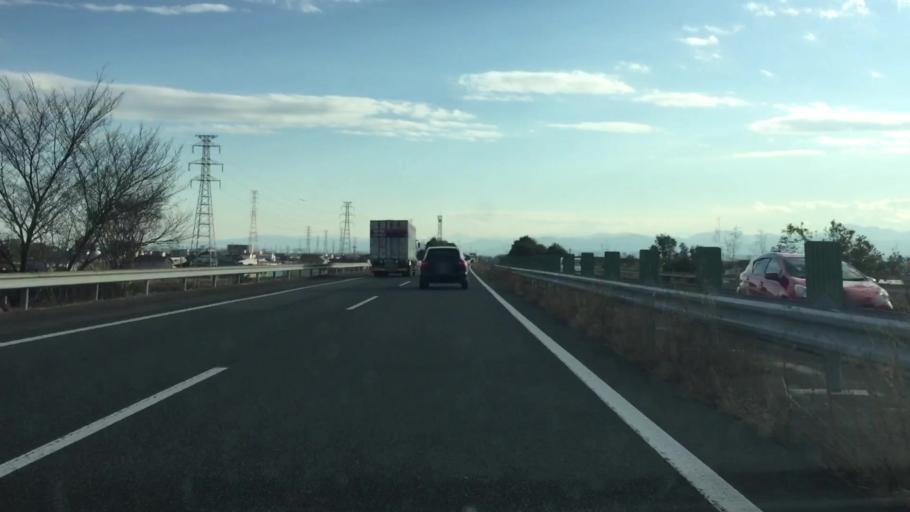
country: JP
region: Gunma
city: Kanekomachi
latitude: 36.4020
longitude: 139.0244
